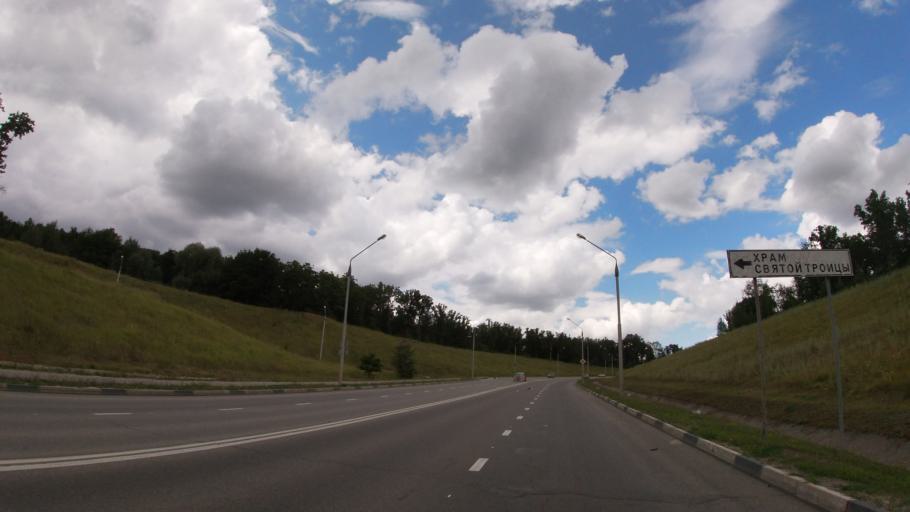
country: RU
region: Belgorod
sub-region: Belgorodskiy Rayon
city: Belgorod
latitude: 50.6223
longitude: 36.6133
